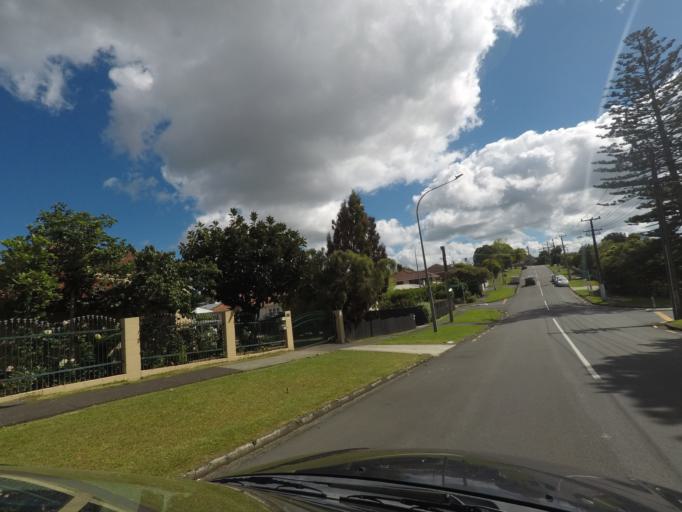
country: NZ
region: Auckland
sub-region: Auckland
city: Waitakere
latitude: -36.9127
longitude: 174.6670
